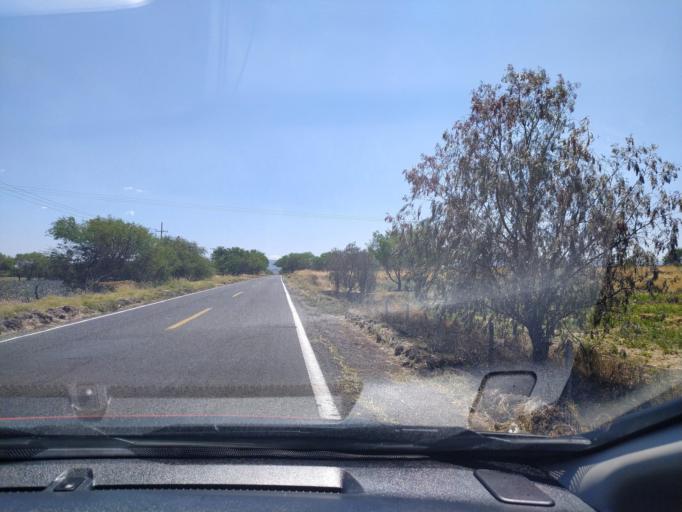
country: MX
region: Guanajuato
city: Ciudad Manuel Doblado
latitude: 20.7658
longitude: -101.8293
